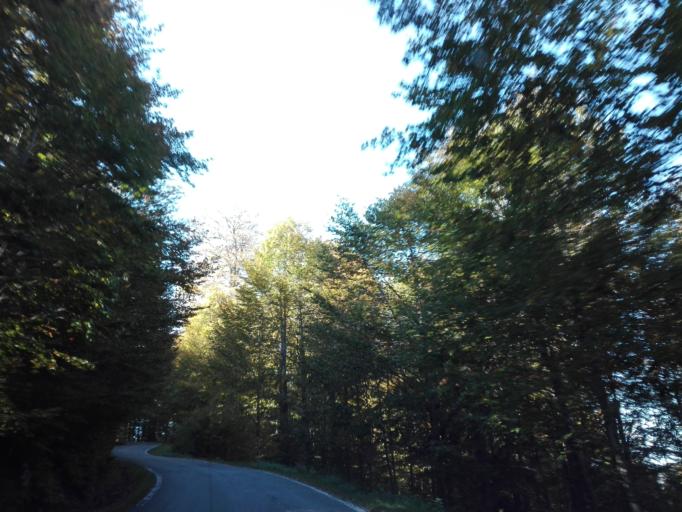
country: ES
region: Navarre
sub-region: Provincia de Navarra
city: Oronz
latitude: 42.9705
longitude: -1.1306
